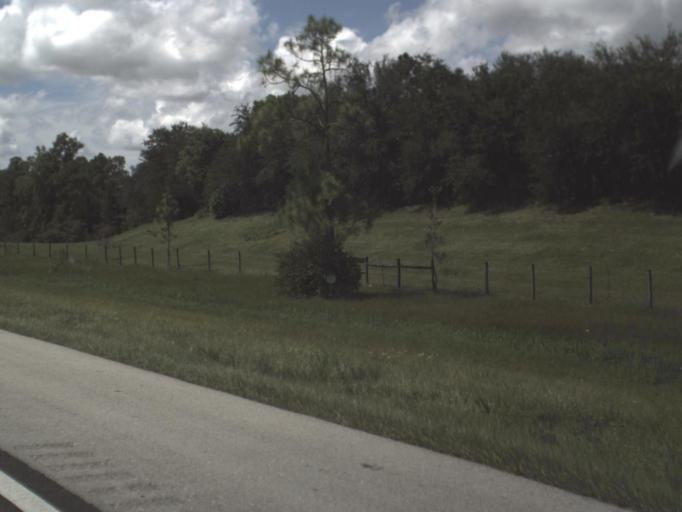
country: US
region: Florida
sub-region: Lee County
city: Gateway
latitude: 26.5536
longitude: -81.7953
